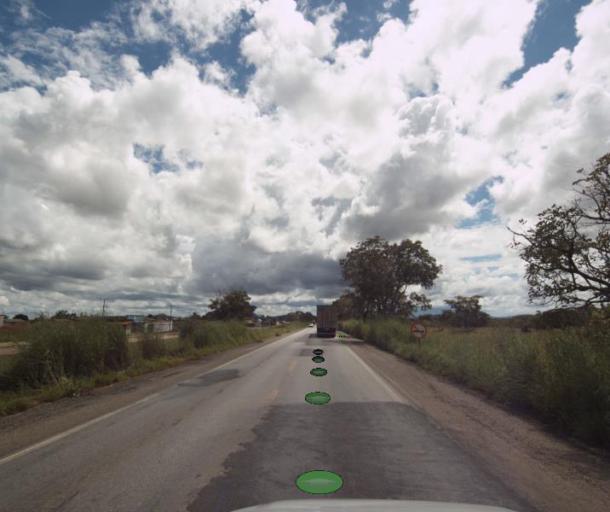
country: BR
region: Goias
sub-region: Uruacu
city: Uruacu
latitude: -14.3089
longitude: -49.1487
